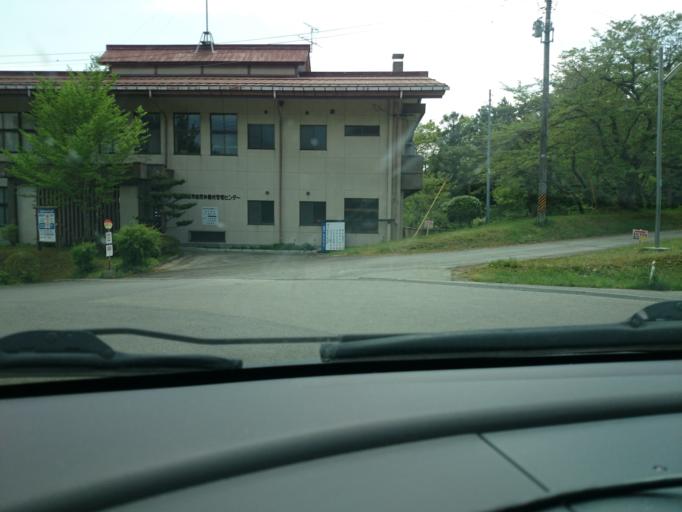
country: JP
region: Fukushima
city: Nihommatsu
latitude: 37.6018
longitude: 140.4266
